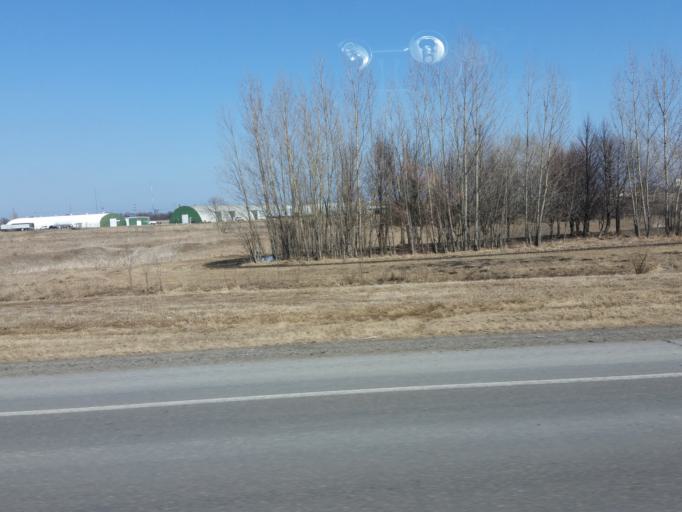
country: US
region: North Dakota
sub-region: Grand Forks County
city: Grand Forks
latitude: 47.9444
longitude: -97.0659
